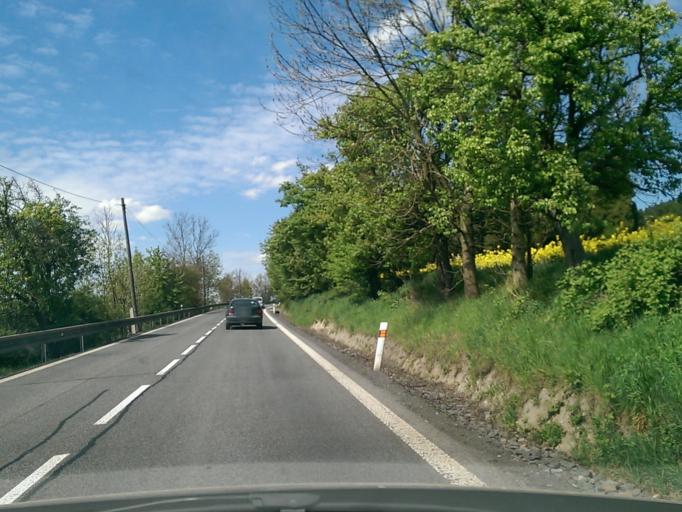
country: CZ
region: Liberecky
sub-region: Okres Semily
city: Turnov
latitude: 50.6101
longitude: 15.1644
